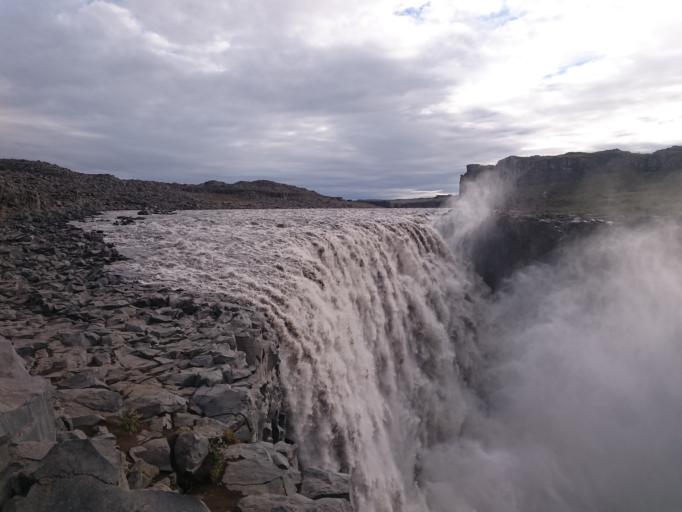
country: IS
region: Northeast
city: Husavik
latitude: 65.8152
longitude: -16.3839
